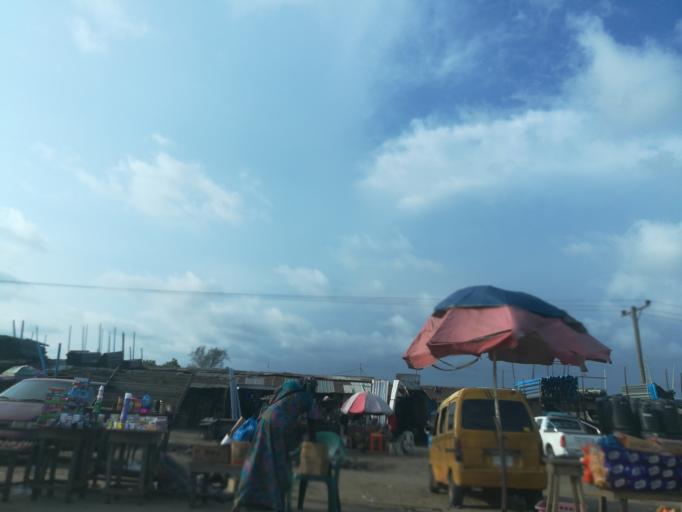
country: NG
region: Ogun
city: Ado Odo
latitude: 6.4816
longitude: 3.0299
